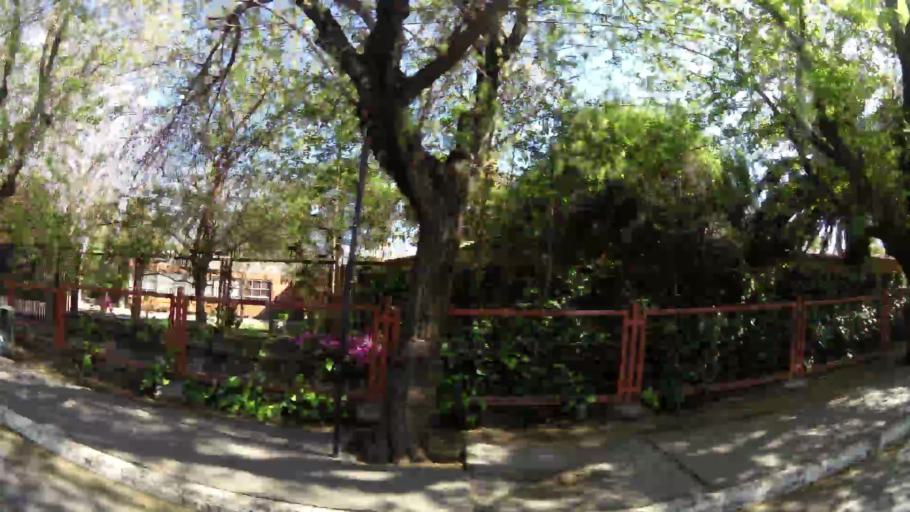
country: CL
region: Santiago Metropolitan
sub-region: Provincia de Santiago
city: Villa Presidente Frei, Nunoa, Santiago, Chile
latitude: -33.4421
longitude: -70.5682
